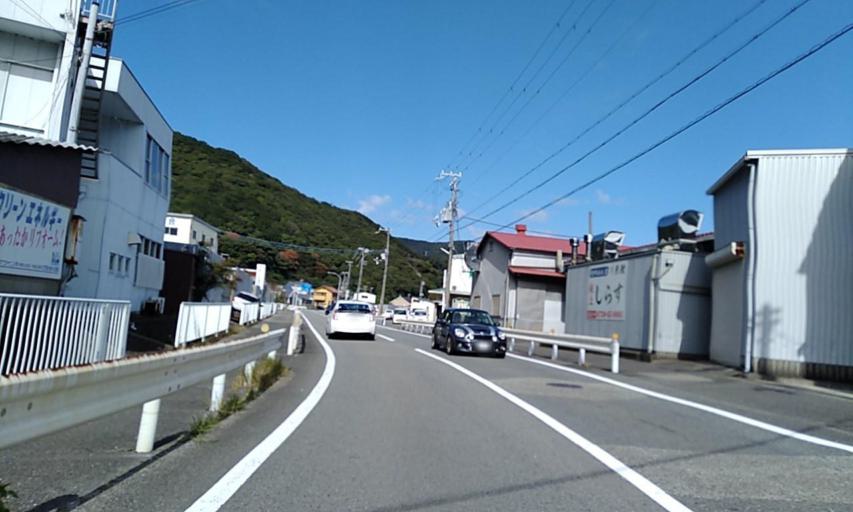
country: JP
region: Wakayama
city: Gobo
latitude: 33.9619
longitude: 135.1235
